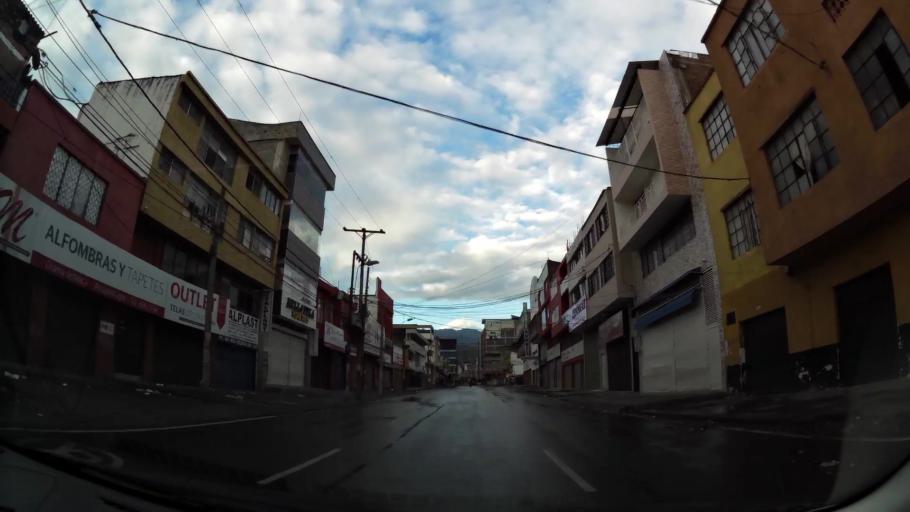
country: CO
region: Valle del Cauca
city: Cali
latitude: 3.4506
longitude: -76.5268
